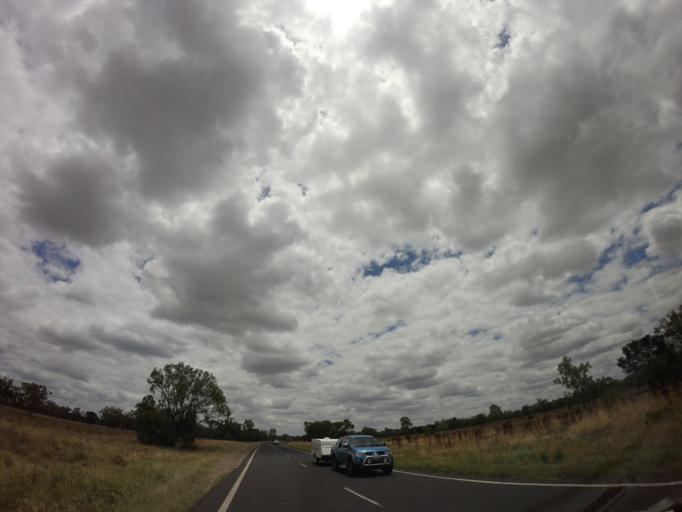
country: AU
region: Queensland
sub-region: Goondiwindi
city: Goondiwindi
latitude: -28.4763
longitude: 150.2929
